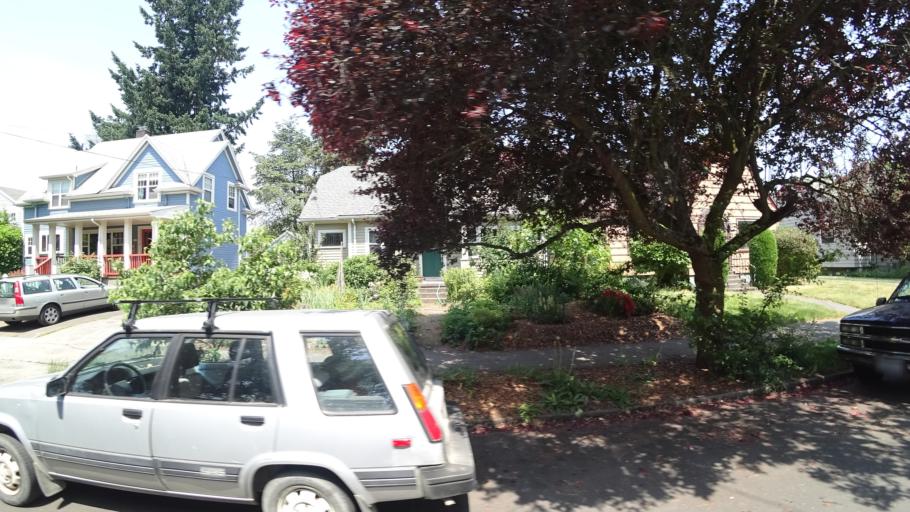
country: US
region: Oregon
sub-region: Multnomah County
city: Portland
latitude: 45.5824
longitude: -122.6855
